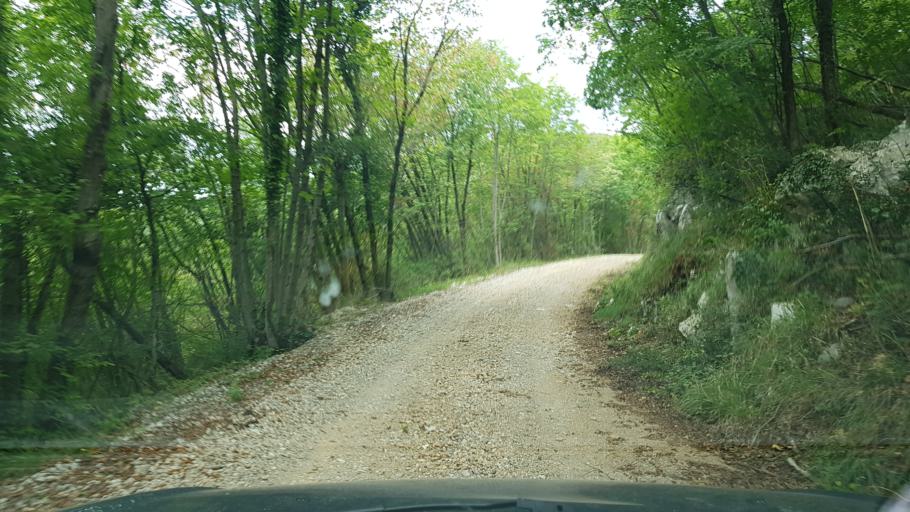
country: SI
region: Kanal
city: Deskle
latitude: 46.0131
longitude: 13.6268
